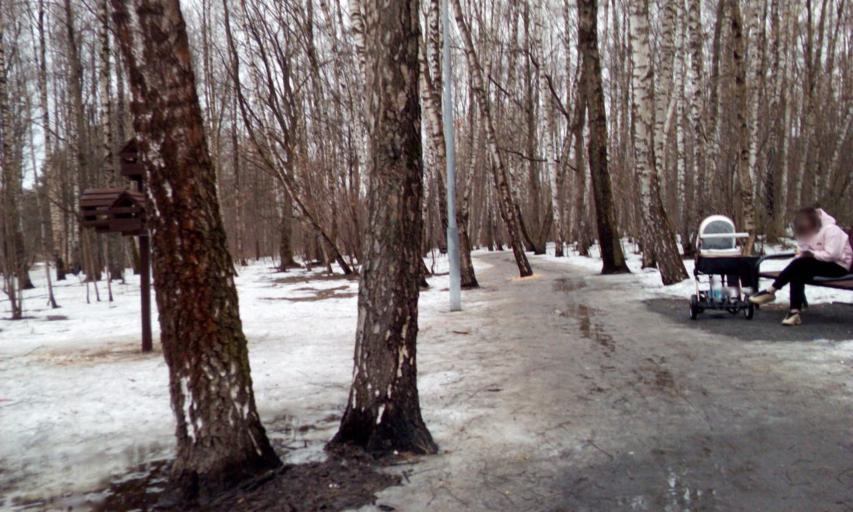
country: RU
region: Moscow
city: Troparevo
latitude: 55.6383
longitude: 37.4812
